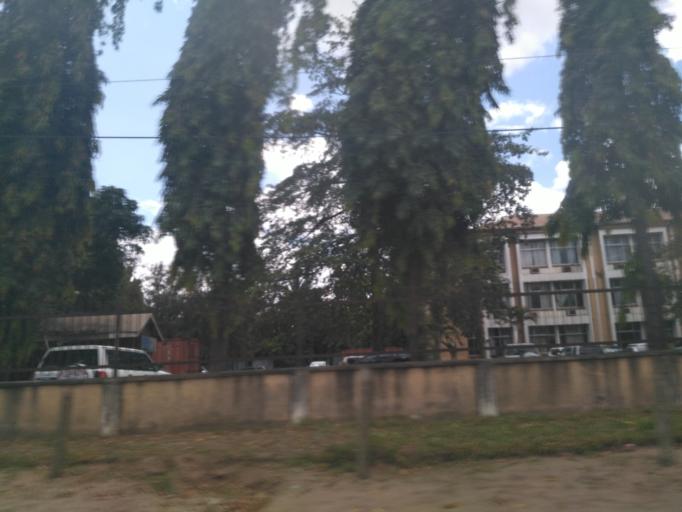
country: TZ
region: Dar es Salaam
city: Dar es Salaam
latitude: -6.8489
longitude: 39.2494
